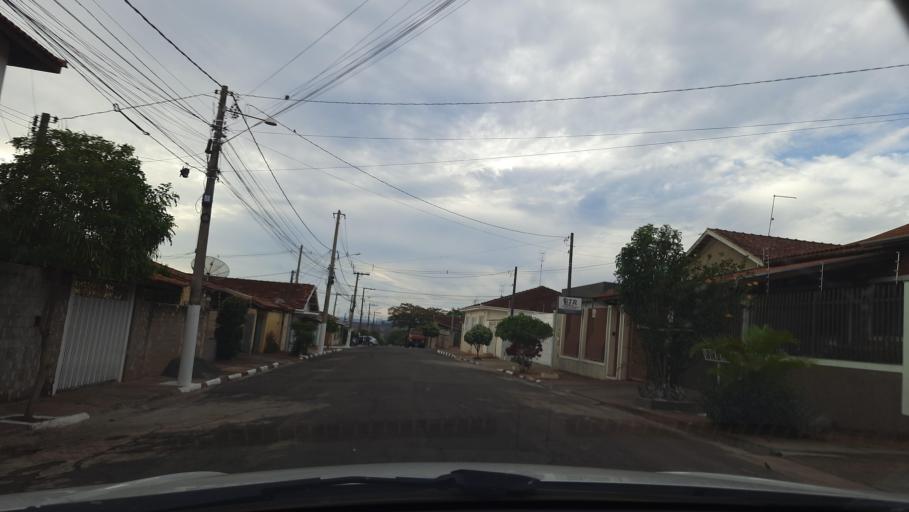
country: BR
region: Sao Paulo
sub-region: Casa Branca
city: Casa Branca
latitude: -21.7840
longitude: -47.0774
